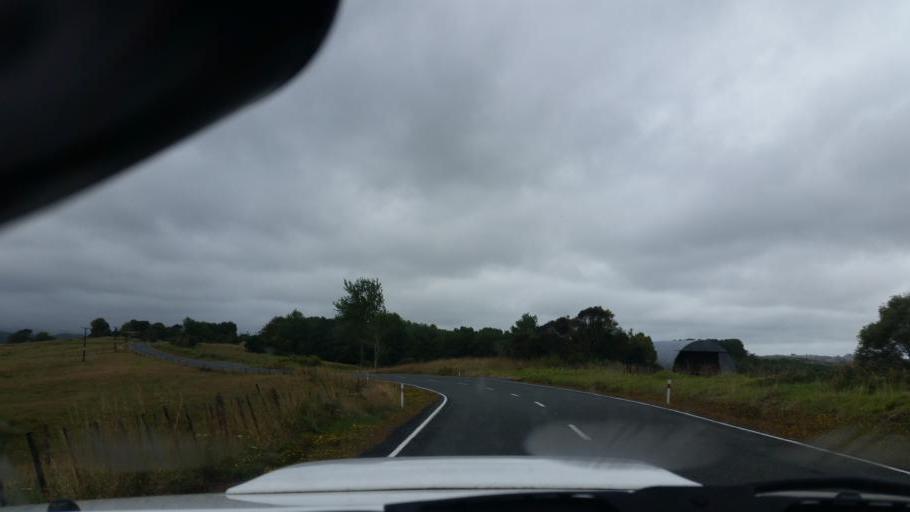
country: NZ
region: Auckland
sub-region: Auckland
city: Wellsford
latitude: -36.1505
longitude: 174.4748
